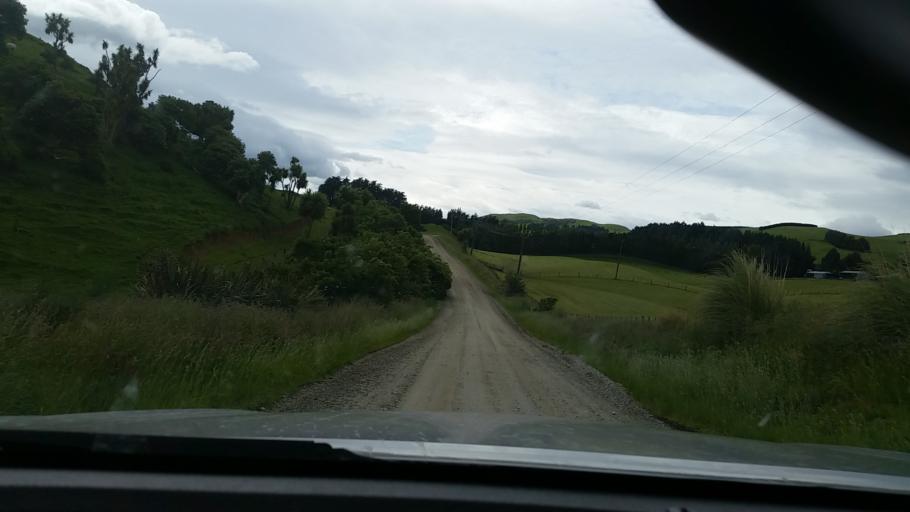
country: NZ
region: Southland
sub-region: Gore District
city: Gore
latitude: -46.2640
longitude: 168.9067
